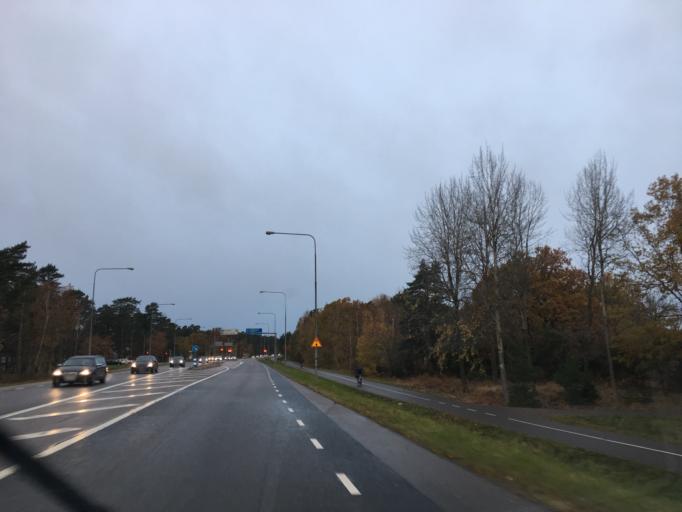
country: SE
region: Kalmar
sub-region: Kalmar Kommun
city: Kalmar
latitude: 56.6774
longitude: 16.3621
